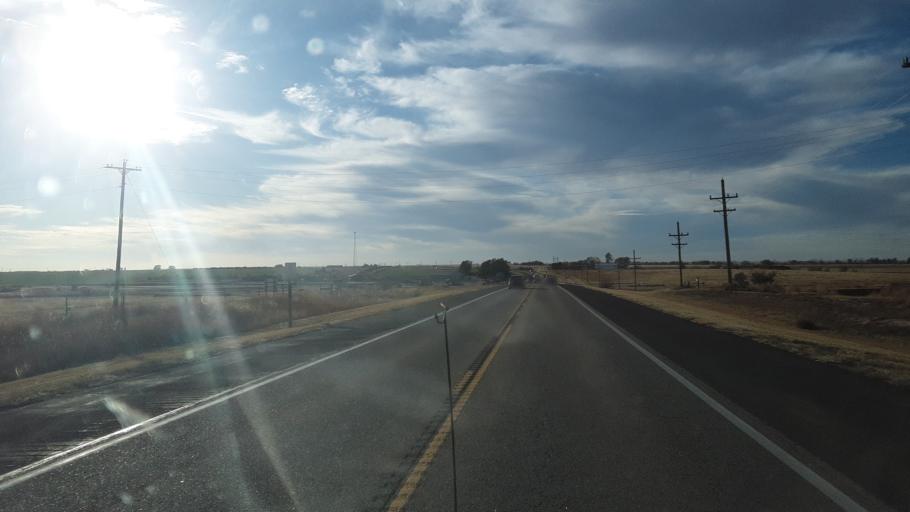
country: US
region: Kansas
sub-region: Kearny County
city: Lakin
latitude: 37.9738
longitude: -101.1807
